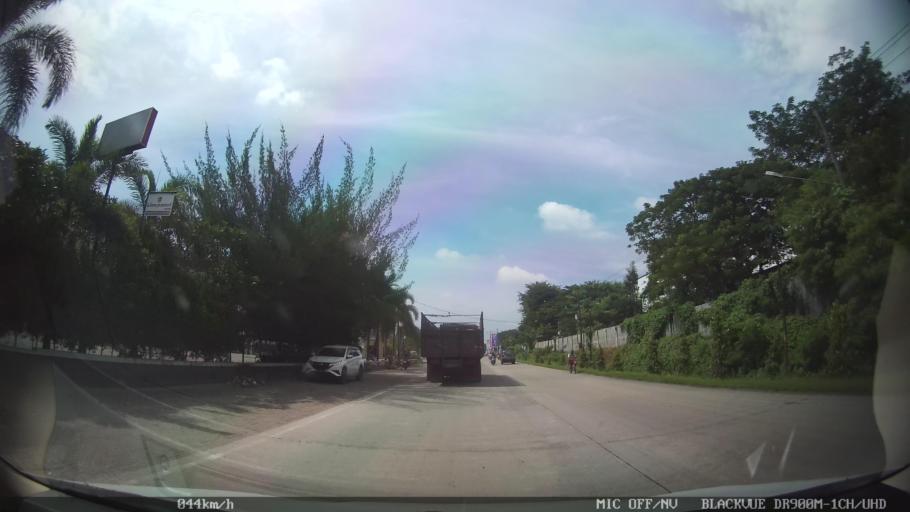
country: ID
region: North Sumatra
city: Medan
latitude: 3.6340
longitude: 98.7081
